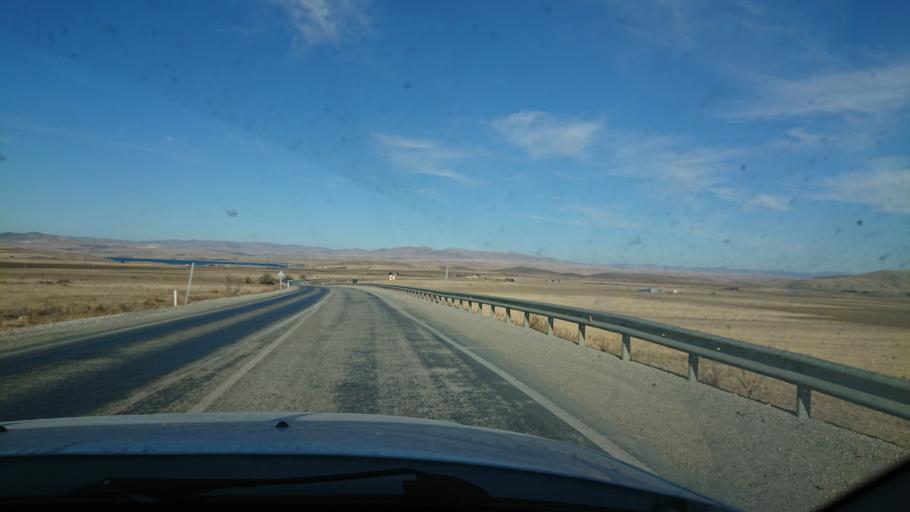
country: TR
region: Aksaray
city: Sariyahsi
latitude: 39.0012
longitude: 33.8552
